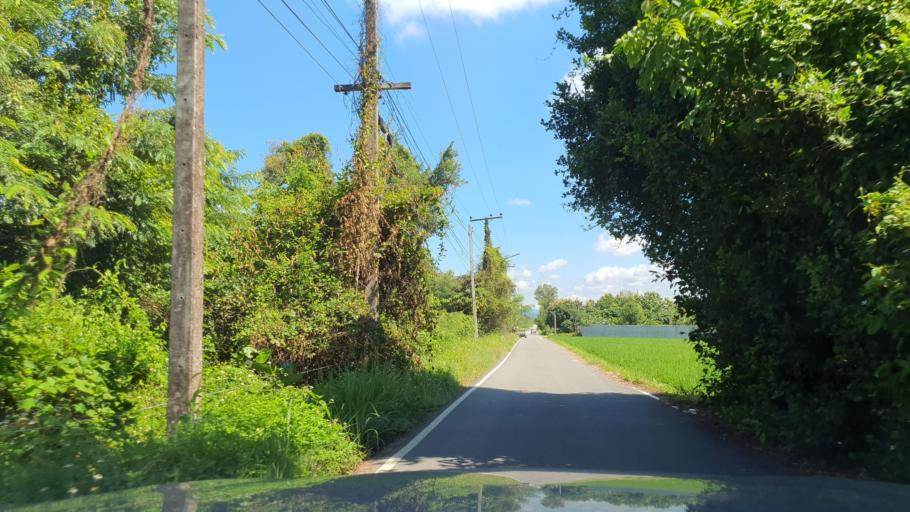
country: TH
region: Chiang Mai
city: San Kamphaeng
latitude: 18.7688
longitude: 99.1693
